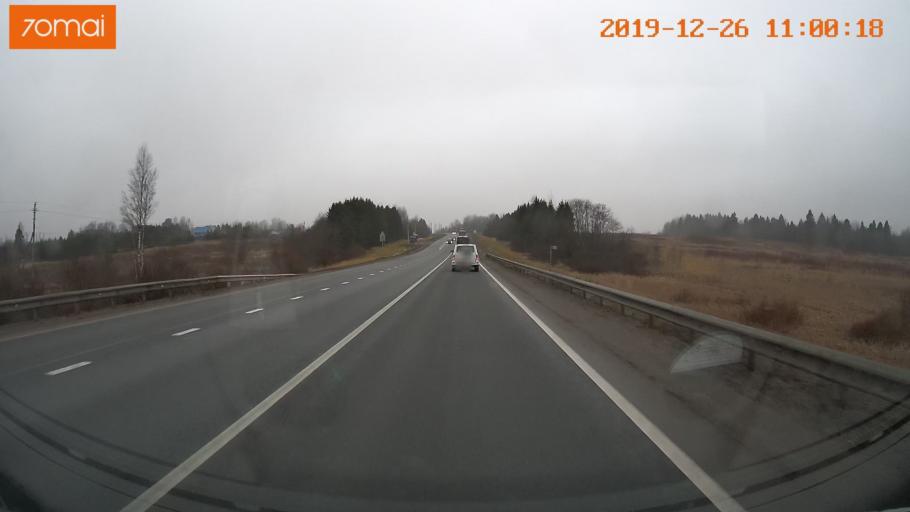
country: RU
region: Vologda
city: Molochnoye
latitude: 59.1680
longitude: 39.4529
